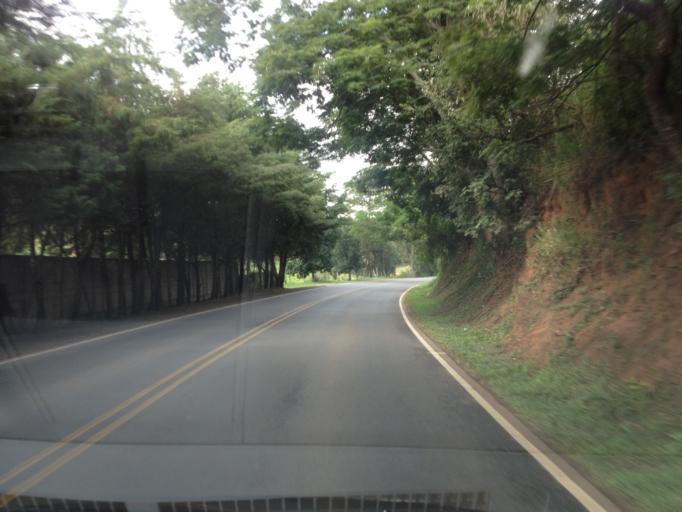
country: BR
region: Minas Gerais
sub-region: Itanhandu
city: Itanhandu
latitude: -22.2218
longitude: -44.9336
